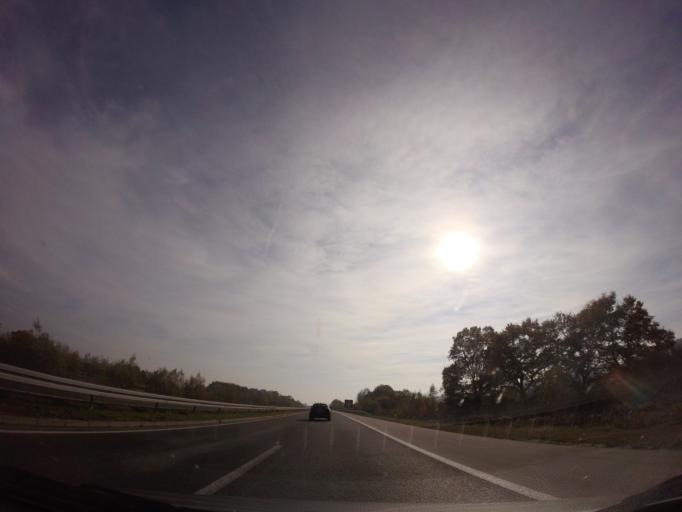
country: HR
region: Zagrebacka
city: Brckovljani
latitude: 45.9366
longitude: 16.2690
